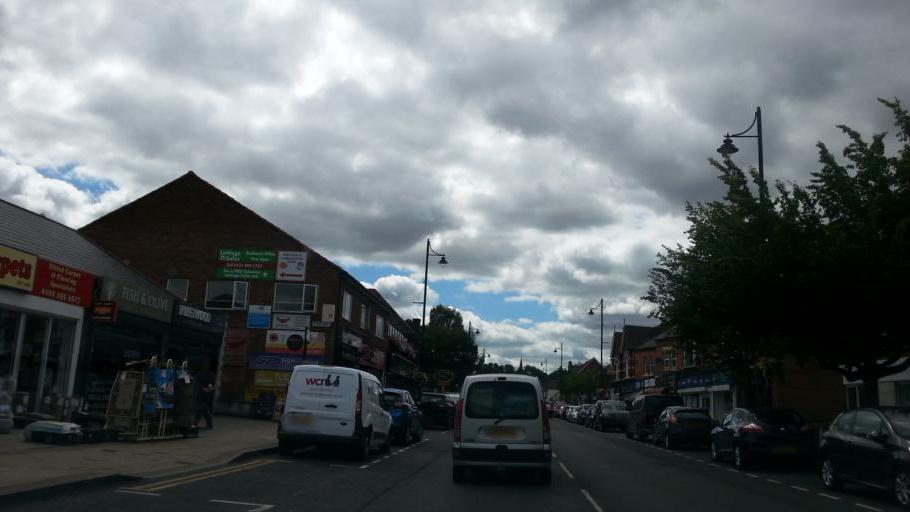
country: GB
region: England
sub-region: City and Borough of Birmingham
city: Sutton Coldfield
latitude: 52.5490
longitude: -1.8413
